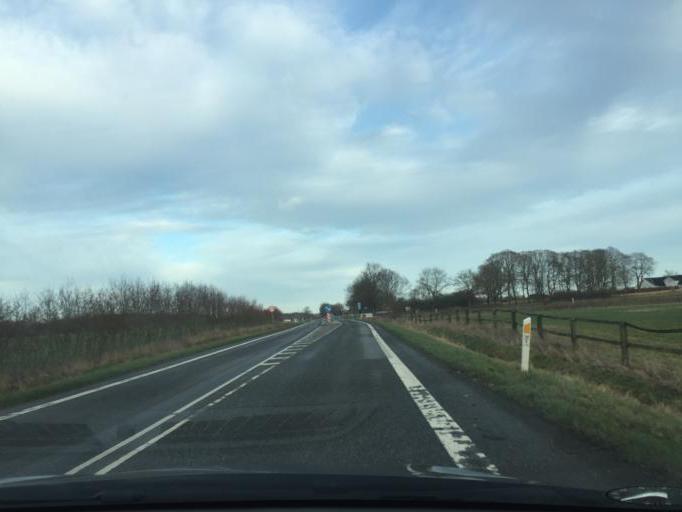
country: DK
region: South Denmark
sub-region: Faaborg-Midtfyn Kommune
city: Ringe
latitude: 55.2196
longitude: 10.4369
